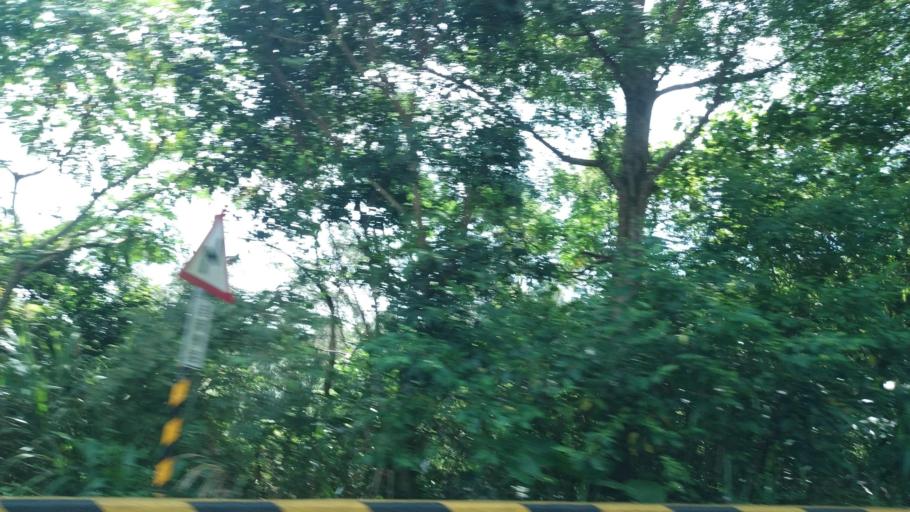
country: TW
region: Taipei
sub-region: Taipei
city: Banqiao
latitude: 24.9452
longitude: 121.5043
